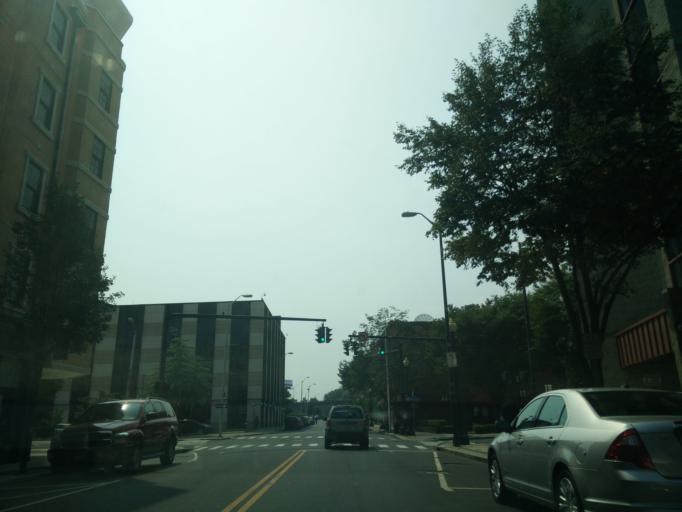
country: US
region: Connecticut
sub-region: Fairfield County
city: Bridgeport
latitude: 41.1785
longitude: -73.1928
